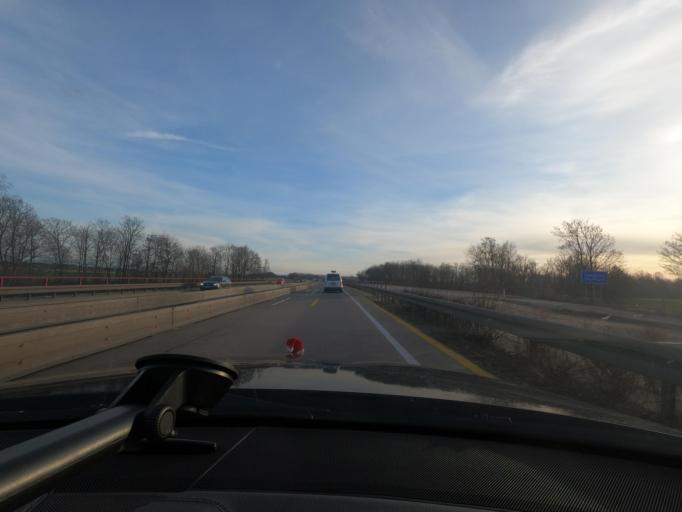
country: DE
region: Lower Saxony
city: Harsum
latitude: 52.2012
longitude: 9.9401
